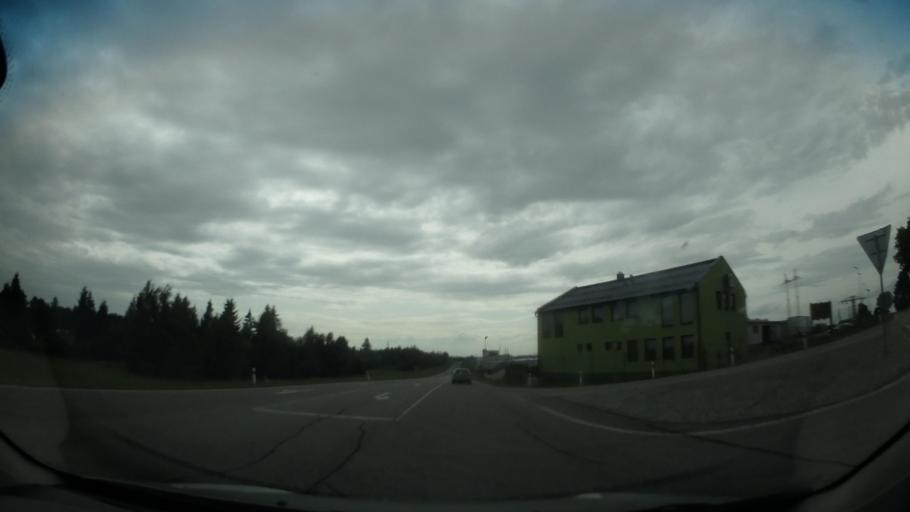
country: CZ
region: Vysocina
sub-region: Okres Zd'ar nad Sazavou
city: Zd'ar nad Sazavou
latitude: 49.5540
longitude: 15.9652
